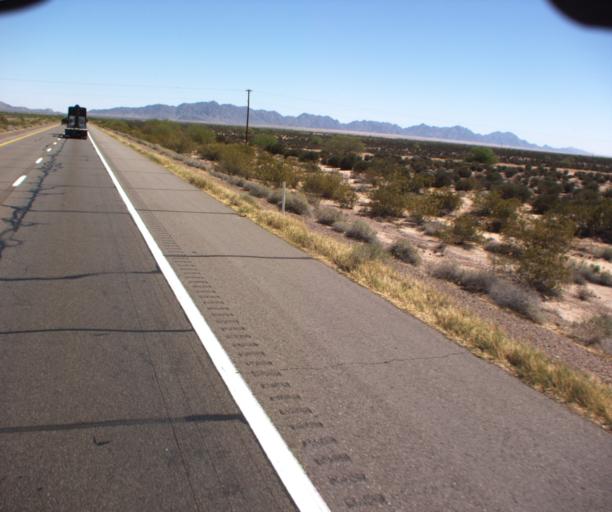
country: US
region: Arizona
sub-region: Yuma County
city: Wellton
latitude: 32.7023
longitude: -113.8943
